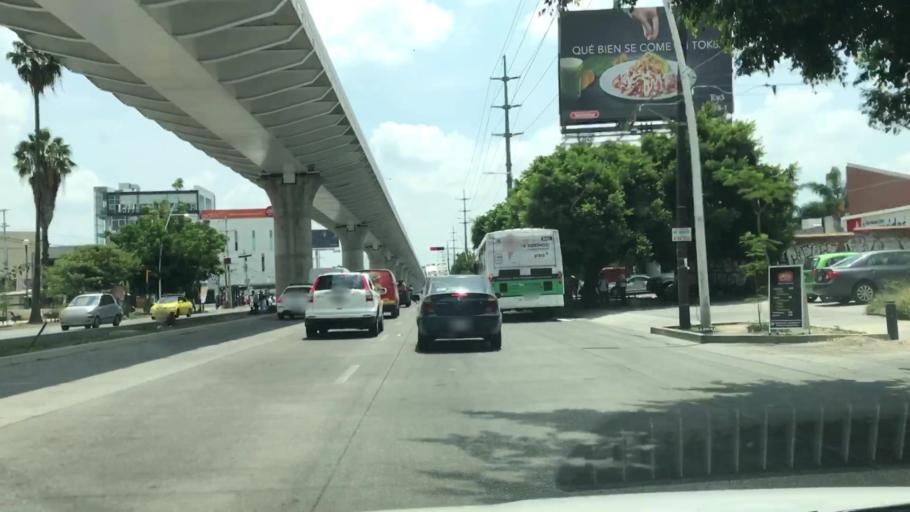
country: MX
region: Jalisco
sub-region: Zapopan
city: Zapopan
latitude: 20.7029
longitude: -103.3606
